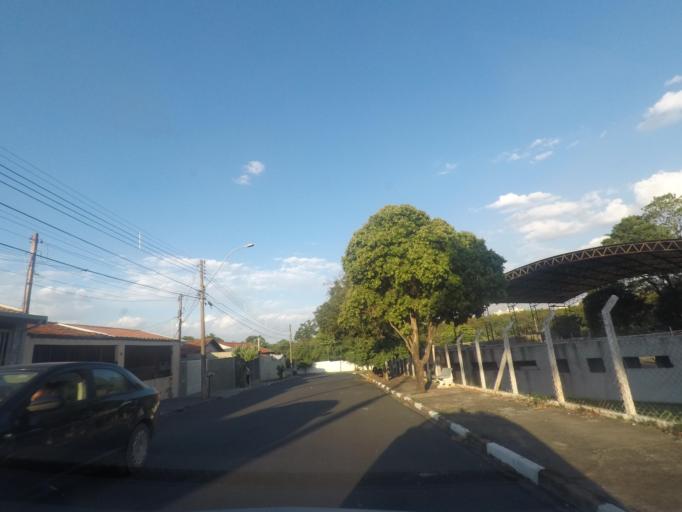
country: BR
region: Sao Paulo
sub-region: Sumare
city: Sumare
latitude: -22.8156
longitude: -47.2801
